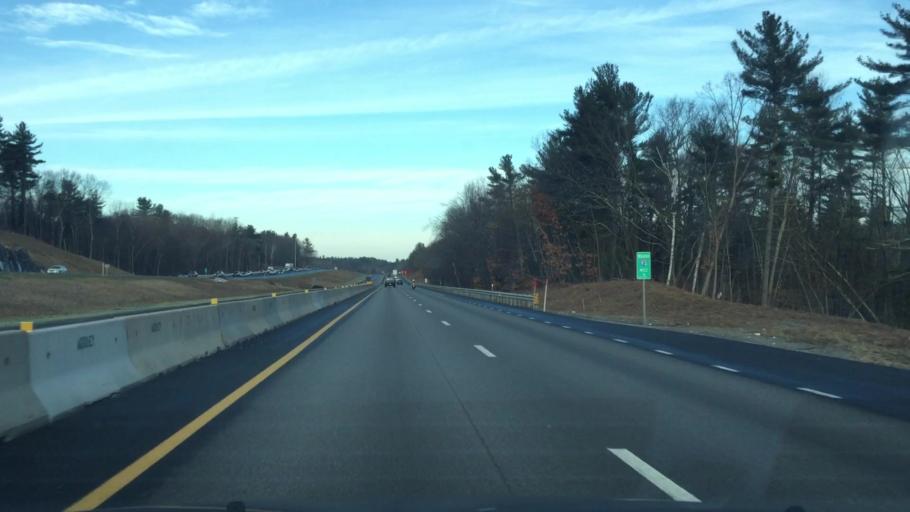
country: US
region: New Hampshire
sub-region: Rockingham County
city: Windham
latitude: 42.8427
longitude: -71.3062
